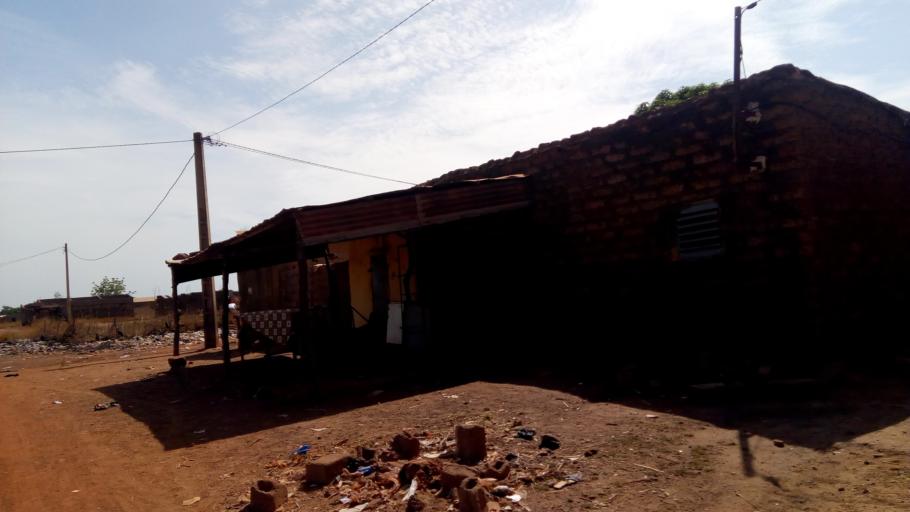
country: ML
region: Koulikoro
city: Kangaba
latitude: 11.9893
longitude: -7.9055
